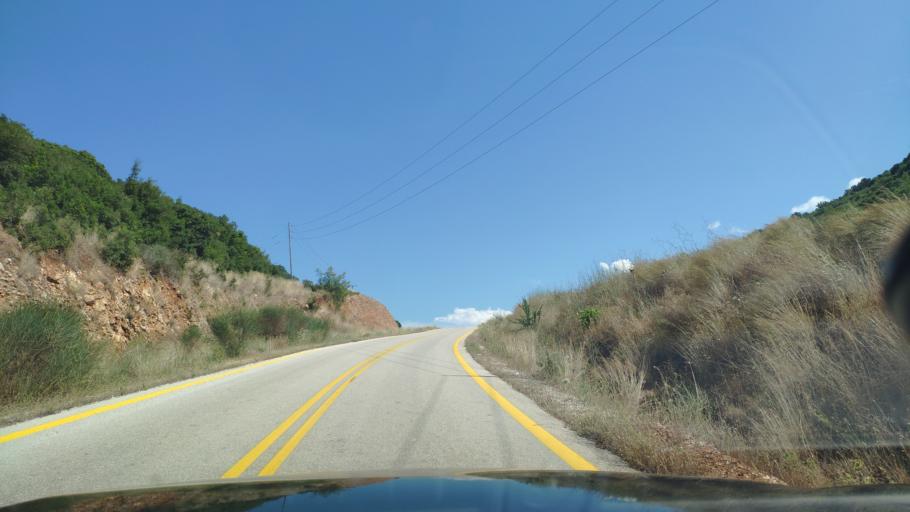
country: GR
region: West Greece
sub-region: Nomos Aitolias kai Akarnanias
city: Katouna
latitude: 38.8577
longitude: 21.0859
